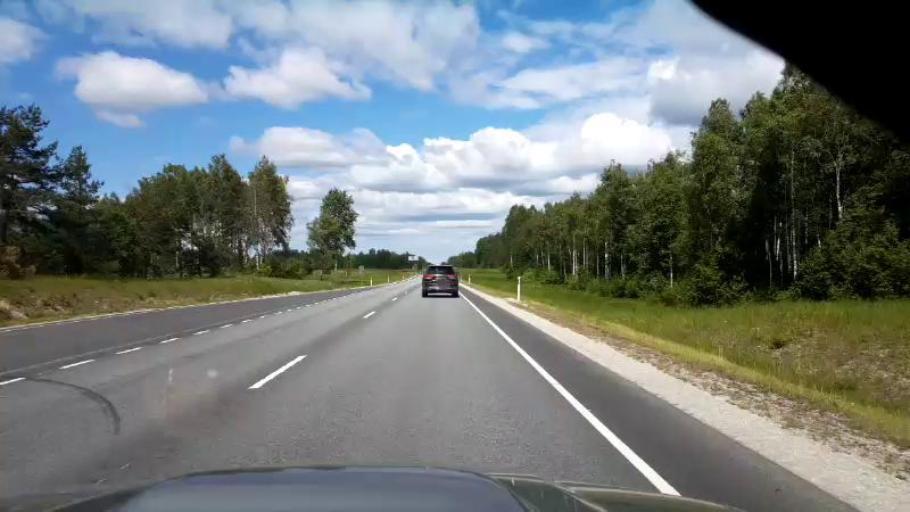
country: EE
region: Harju
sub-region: Nissi vald
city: Riisipere
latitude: 59.0823
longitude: 24.4579
